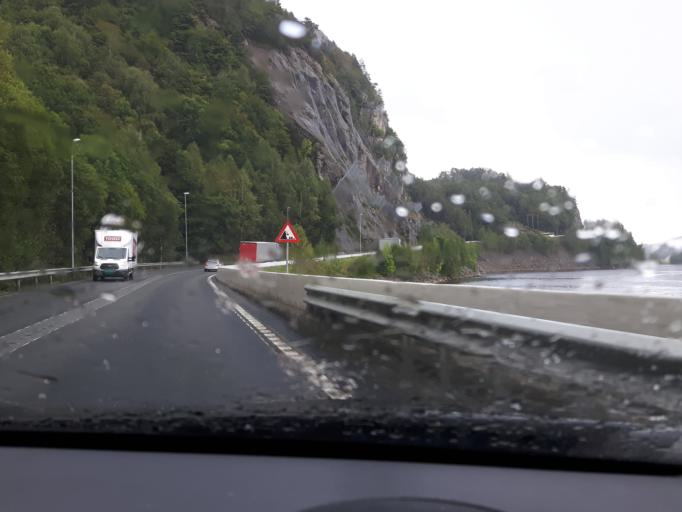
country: NO
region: Vest-Agder
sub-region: Sogne
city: Sogne
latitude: 58.1028
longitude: 7.6673
